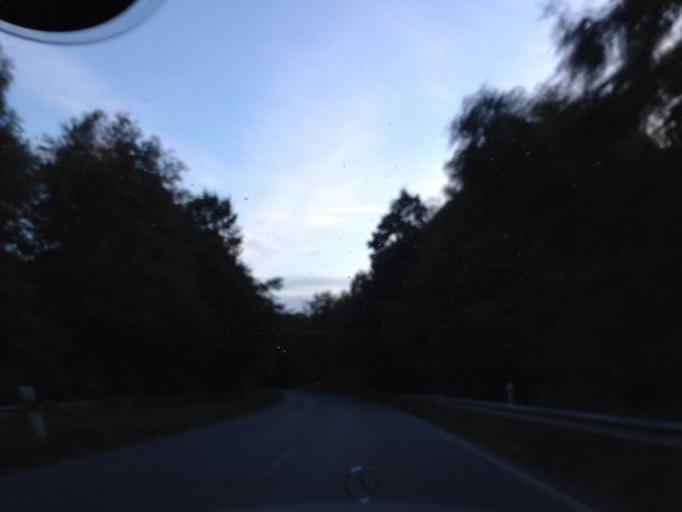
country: DE
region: Schleswig-Holstein
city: Hammoor
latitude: 53.7014
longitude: 10.2983
